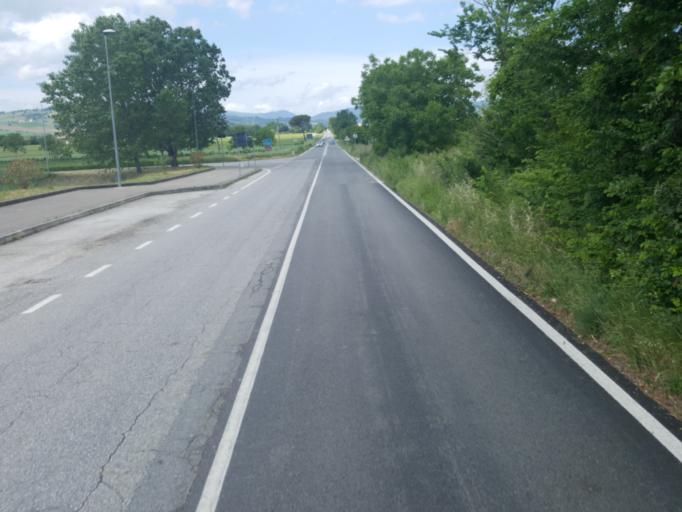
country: IT
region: The Marches
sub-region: Provincia di Macerata
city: Pollenza
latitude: 43.2391
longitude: 13.3669
